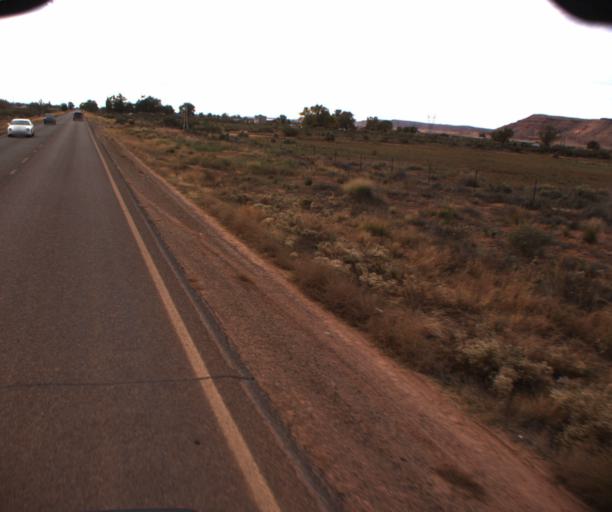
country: US
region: Arizona
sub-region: Apache County
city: Many Farms
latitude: 36.2484
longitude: -109.6045
